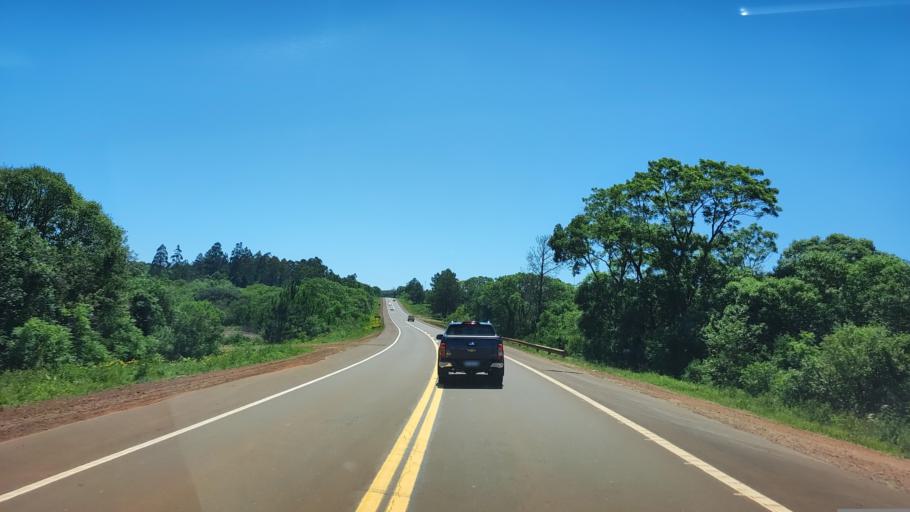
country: AR
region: Misiones
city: Aristobulo del Valle
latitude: -27.0872
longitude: -54.7857
